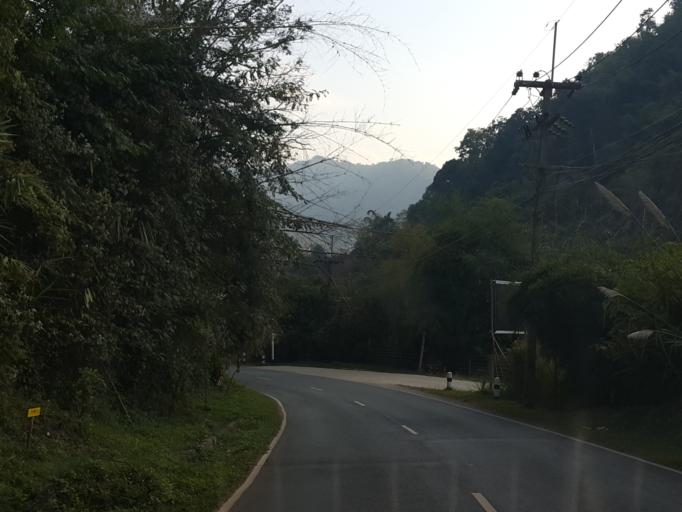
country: TH
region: Chiang Mai
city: Samoeng
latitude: 18.9004
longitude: 98.8318
